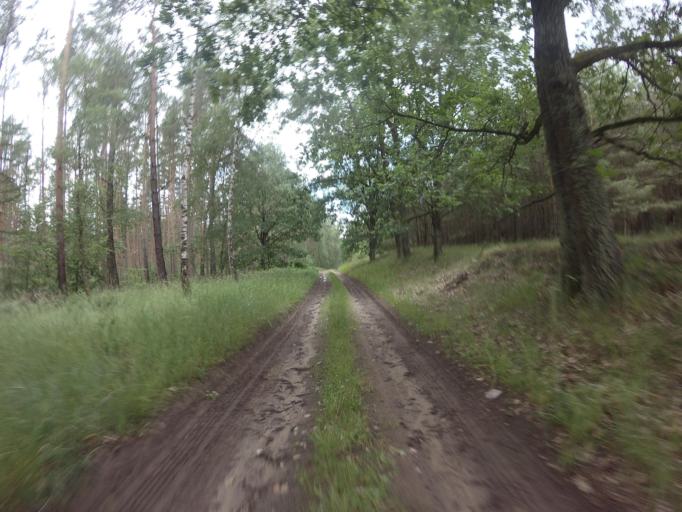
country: PL
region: West Pomeranian Voivodeship
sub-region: Powiat choszczenski
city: Krzecin
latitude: 53.0396
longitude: 15.5654
